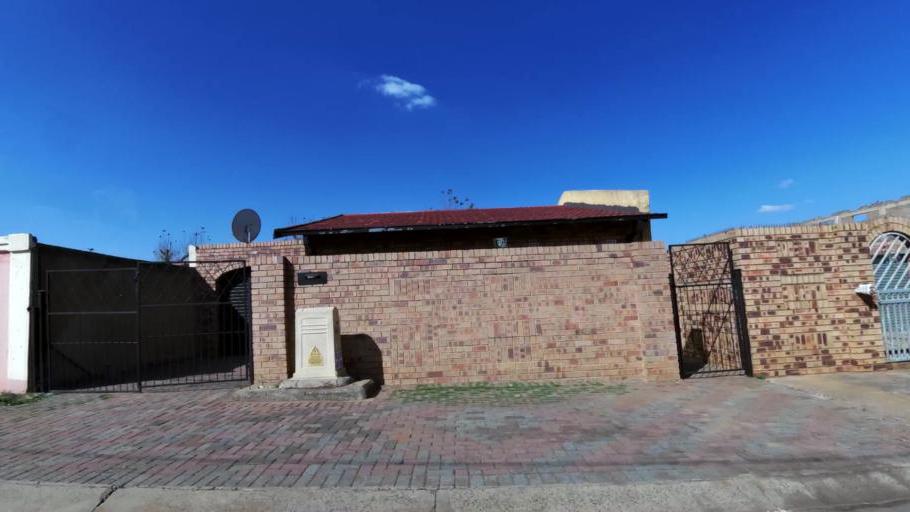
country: ZA
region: Gauteng
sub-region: City of Johannesburg Metropolitan Municipality
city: Soweto
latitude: -26.2378
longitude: 27.8820
